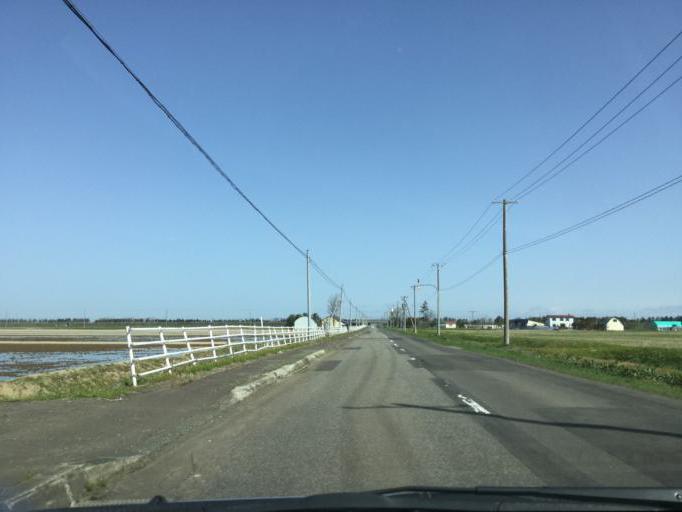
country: JP
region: Hokkaido
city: Iwamizawa
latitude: 43.1483
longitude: 141.7183
